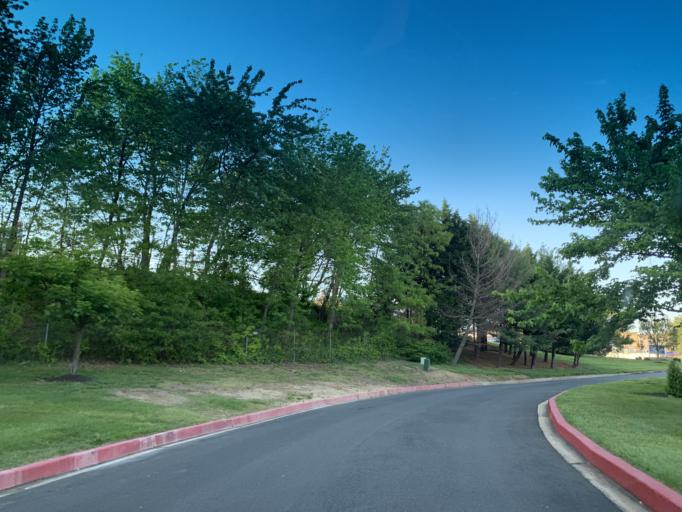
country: US
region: Maryland
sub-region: Harford County
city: Aberdeen
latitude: 39.5217
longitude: -76.1910
